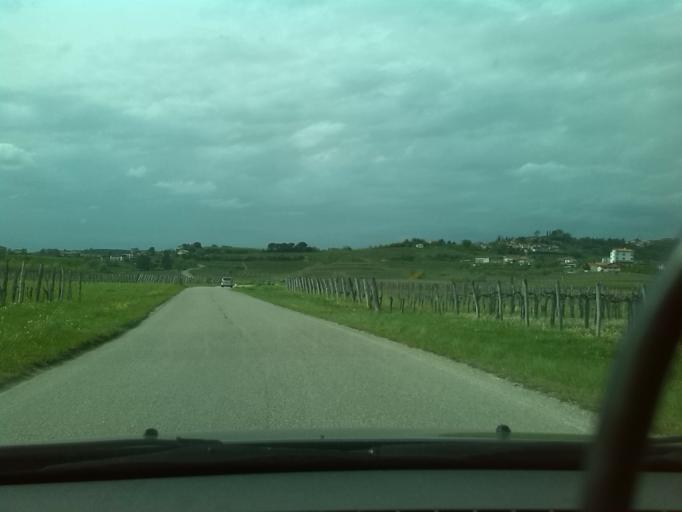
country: SI
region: Brda
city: Dobrovo
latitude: 45.9685
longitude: 13.5225
